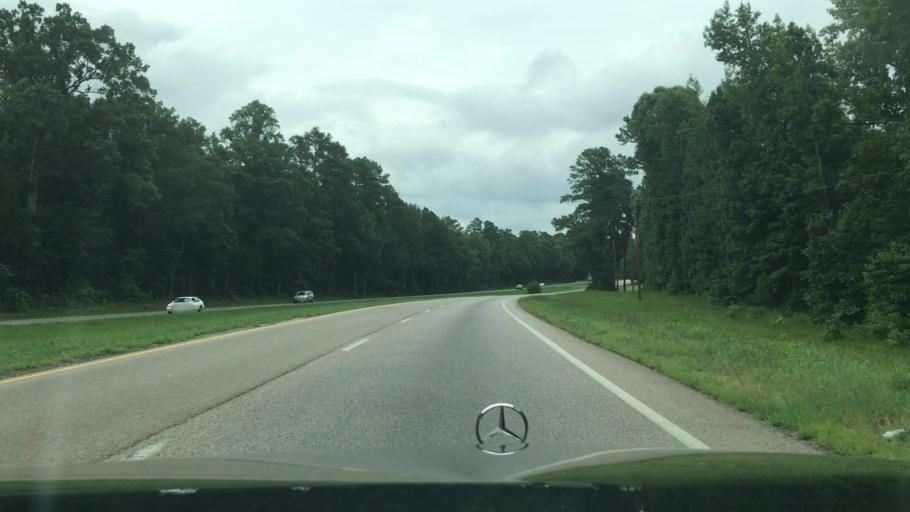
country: US
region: Virginia
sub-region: Amelia County
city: Amelia Court House
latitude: 37.3580
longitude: -77.8336
